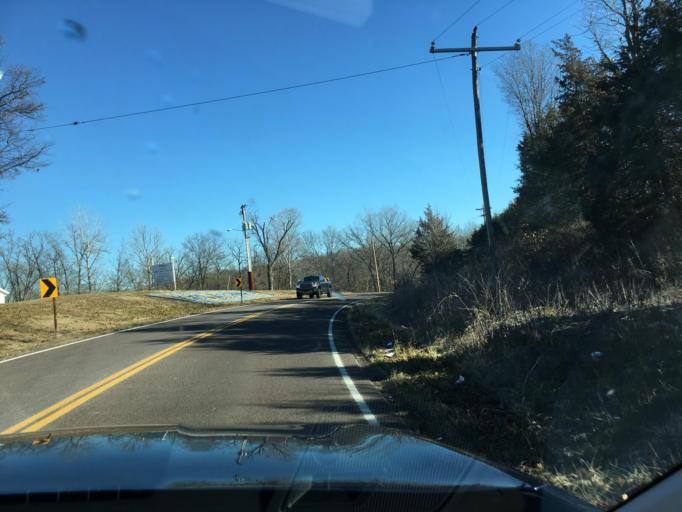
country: US
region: Missouri
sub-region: Jefferson County
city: De Soto
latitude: 38.1529
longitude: -90.5448
